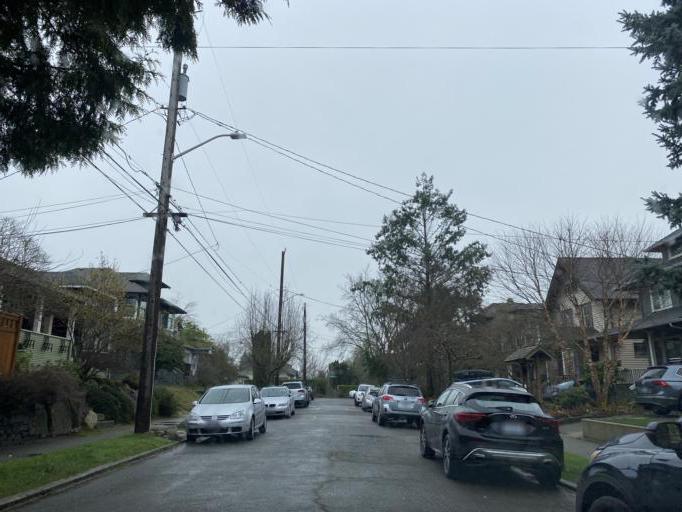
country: US
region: Washington
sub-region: King County
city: Seattle
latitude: 47.6092
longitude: -122.2926
